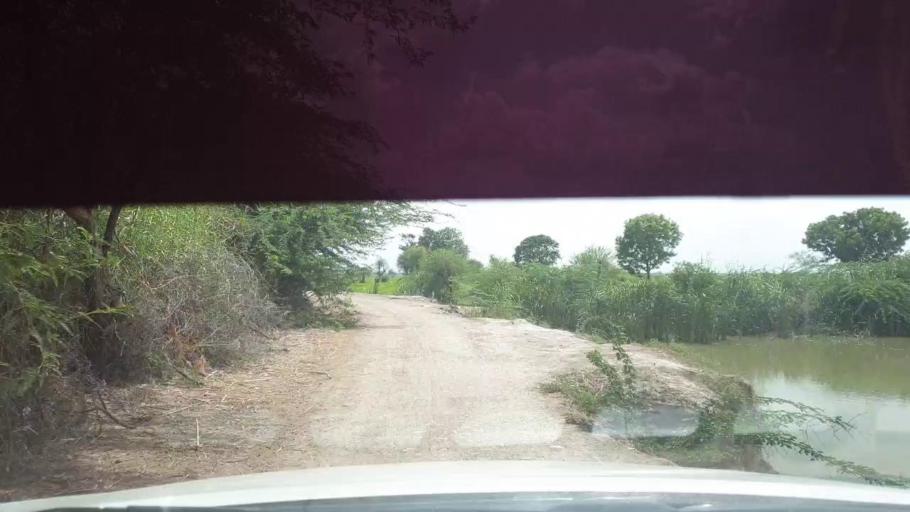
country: PK
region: Sindh
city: Kadhan
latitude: 24.6166
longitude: 69.0259
